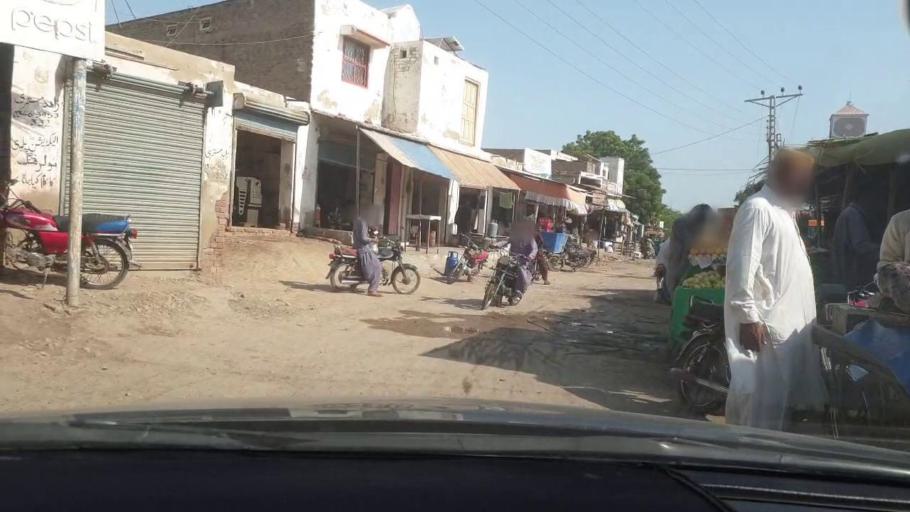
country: PK
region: Sindh
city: Naukot
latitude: 24.7624
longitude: 69.1995
